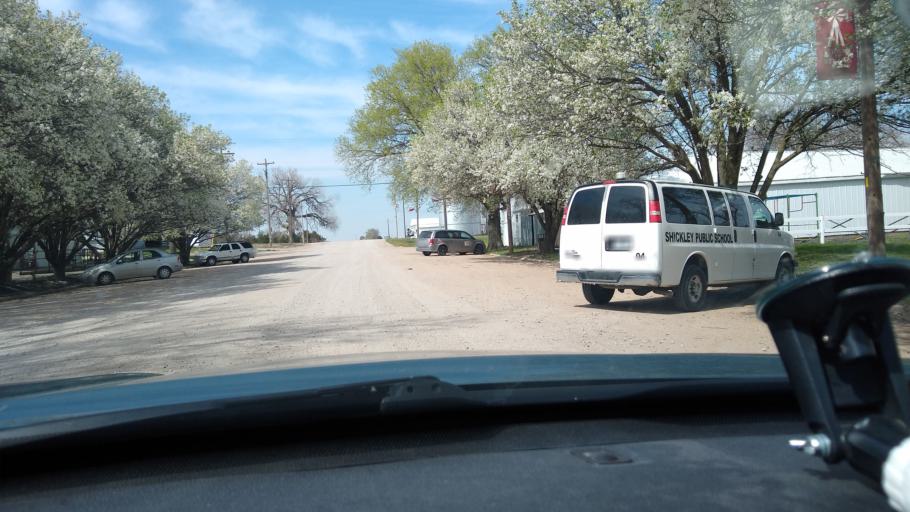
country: US
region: Nebraska
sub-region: Fillmore County
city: Geneva
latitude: 40.4148
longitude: -97.5868
